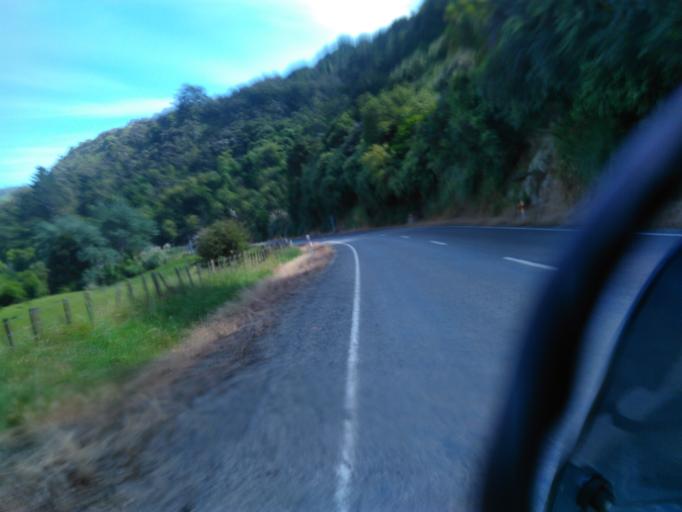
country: NZ
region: Hawke's Bay
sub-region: Wairoa District
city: Wairoa
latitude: -38.8663
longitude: 177.1990
